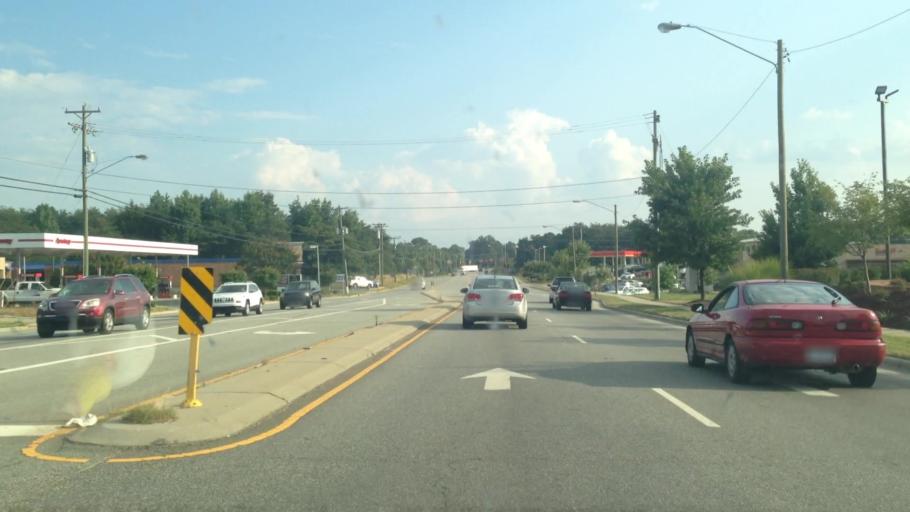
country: US
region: North Carolina
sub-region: Forsyth County
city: Kernersville
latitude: 36.0903
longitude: -80.0623
